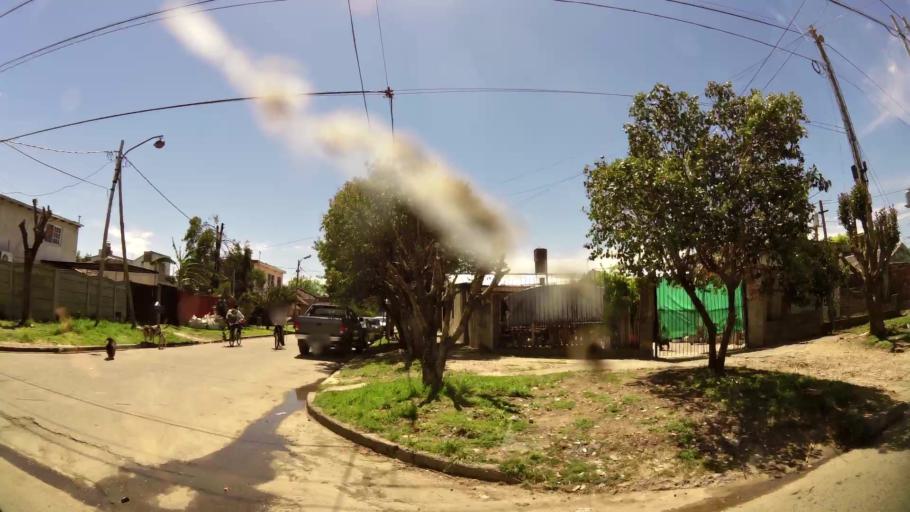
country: AR
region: Buenos Aires
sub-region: Partido de Quilmes
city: Quilmes
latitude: -34.7366
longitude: -58.3005
